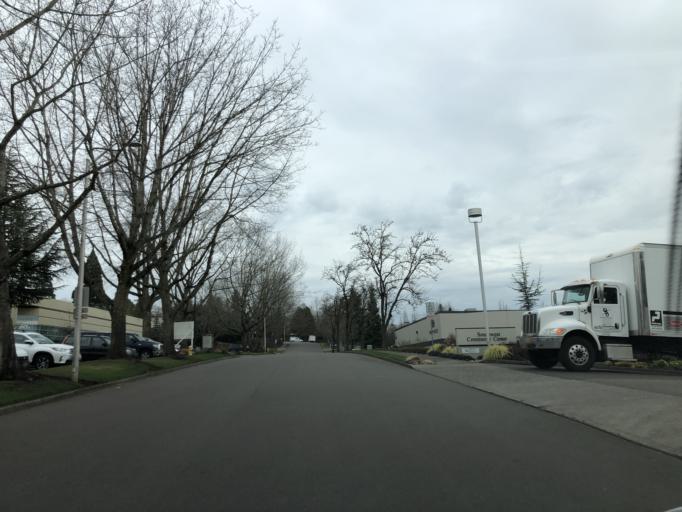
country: US
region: Oregon
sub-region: Washington County
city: Durham
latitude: 45.4200
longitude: -122.7548
